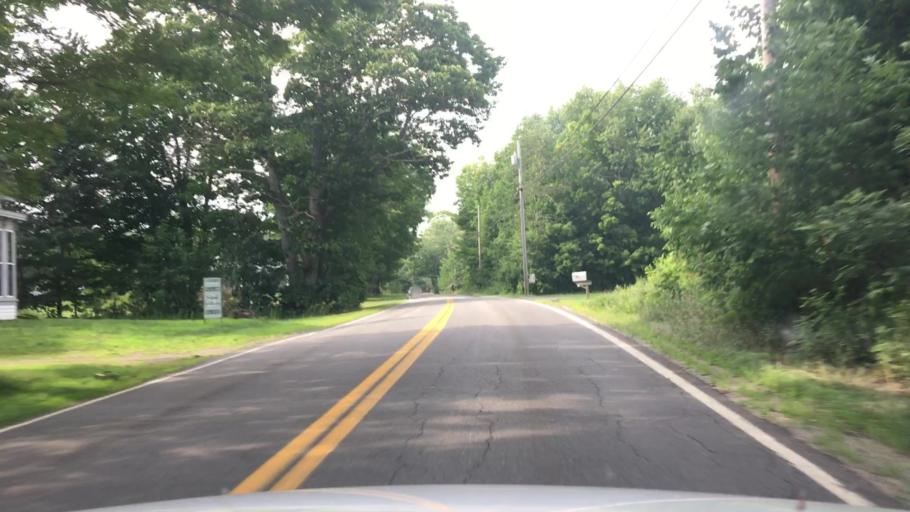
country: US
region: Maine
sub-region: Lincoln County
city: Waldoboro
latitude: 44.1480
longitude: -69.3741
